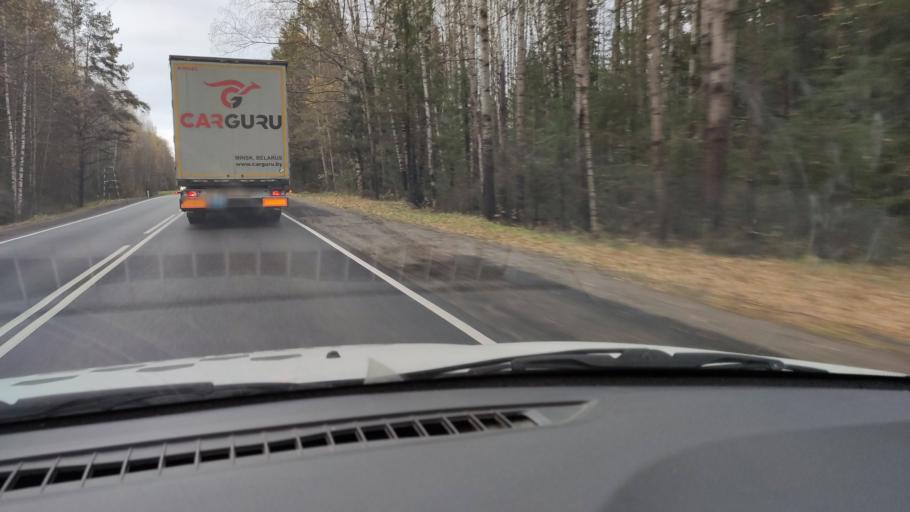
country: RU
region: Kirov
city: Belaya Kholunitsa
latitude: 58.8255
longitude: 50.6242
